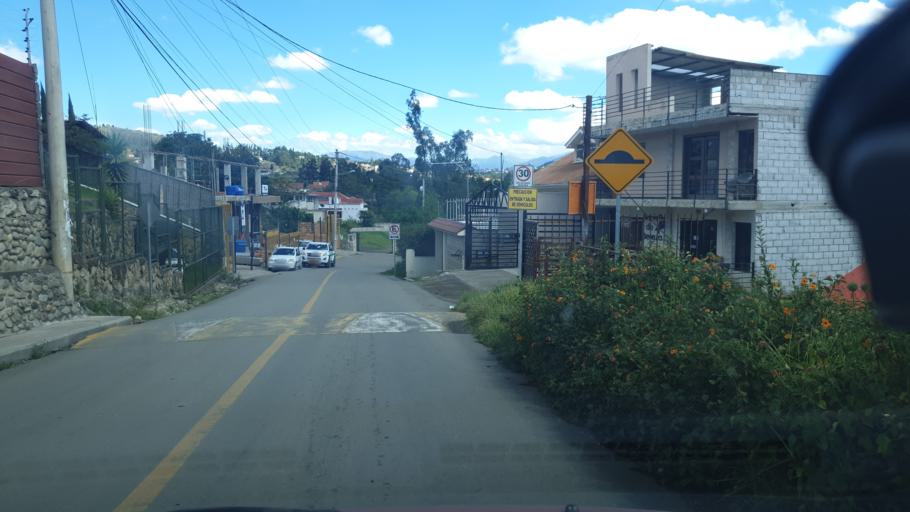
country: EC
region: Azuay
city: Llacao
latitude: -2.8559
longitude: -78.9093
